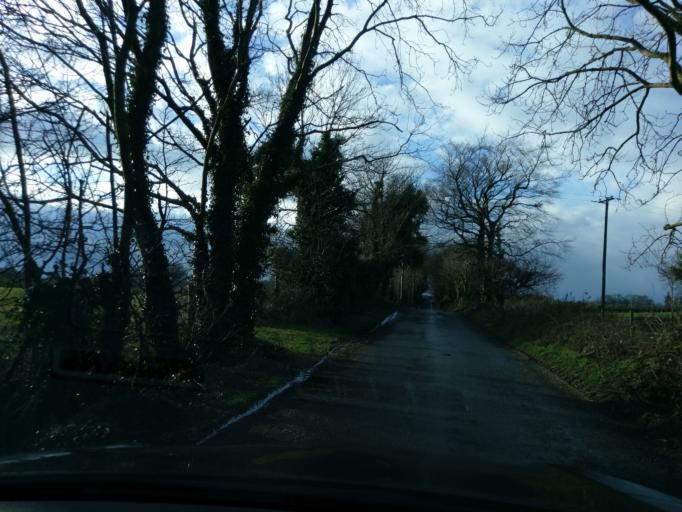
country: IE
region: Connaught
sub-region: County Galway
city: Athenry
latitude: 53.3875
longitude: -8.6030
